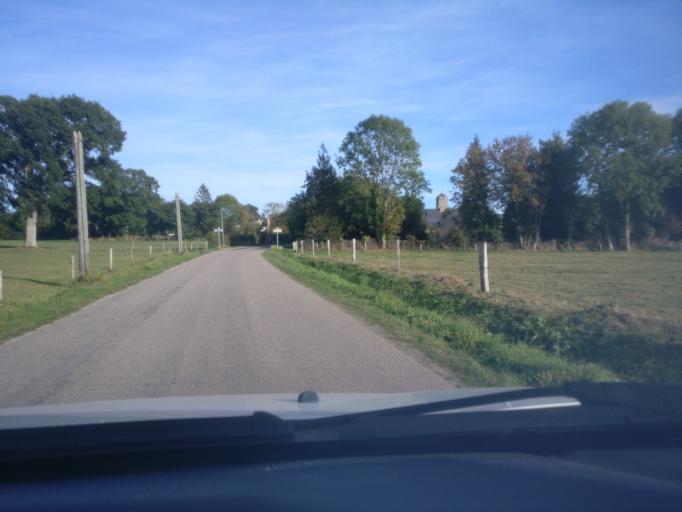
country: FR
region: Lower Normandy
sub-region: Departement de la Manche
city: Sartilly
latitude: 48.7023
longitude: -1.4449
